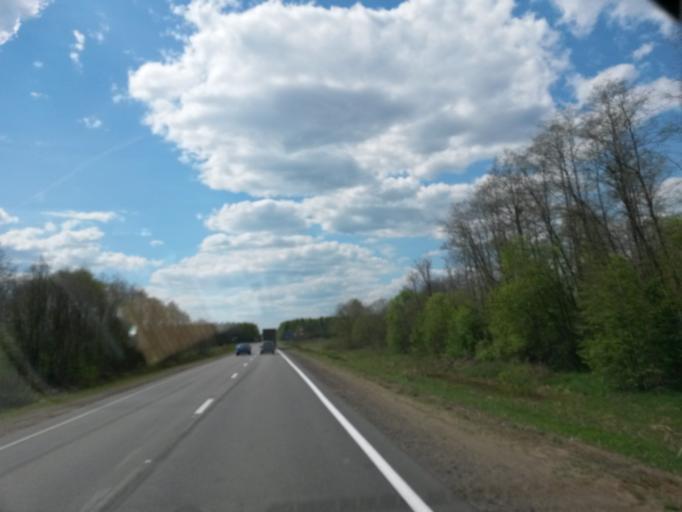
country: RU
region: Jaroslavl
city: Bol'shoye Selo
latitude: 57.7241
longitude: 38.8860
